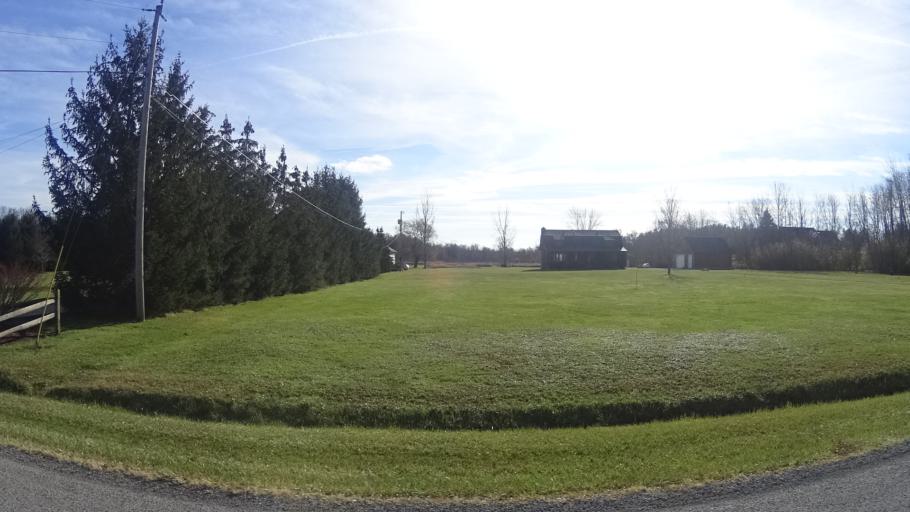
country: US
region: Ohio
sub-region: Lorain County
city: Eaton Estates
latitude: 41.2943
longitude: -81.9931
